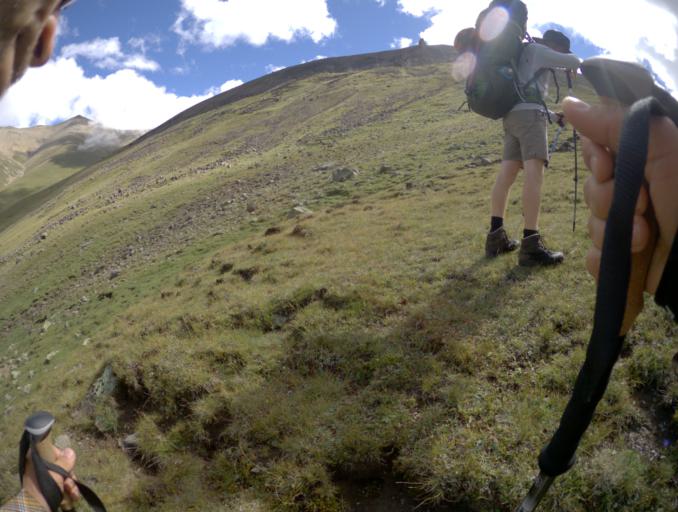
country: RU
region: Kabardino-Balkariya
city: Terskol
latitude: 43.3903
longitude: 42.3622
